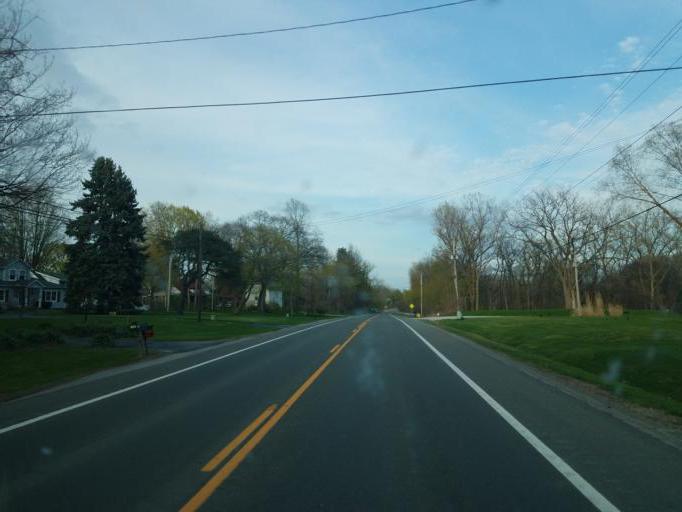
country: US
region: Ohio
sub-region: Erie County
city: Huron
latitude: 41.3804
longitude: -82.4795
